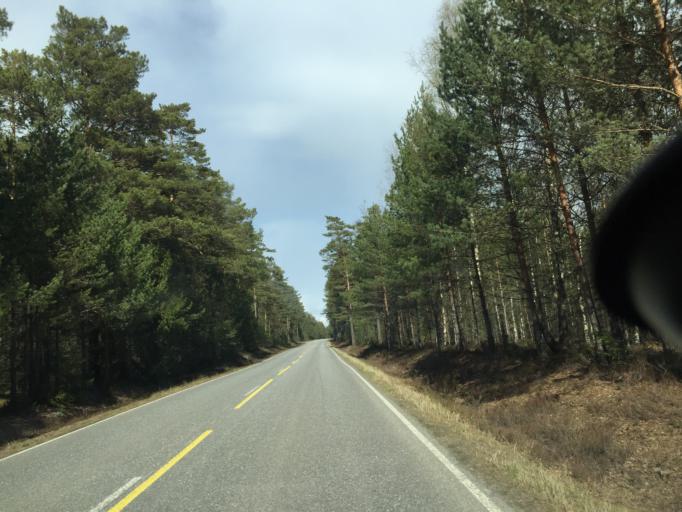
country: FI
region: Uusimaa
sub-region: Raaseporin
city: Hanko
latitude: 59.9554
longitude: 22.9631
